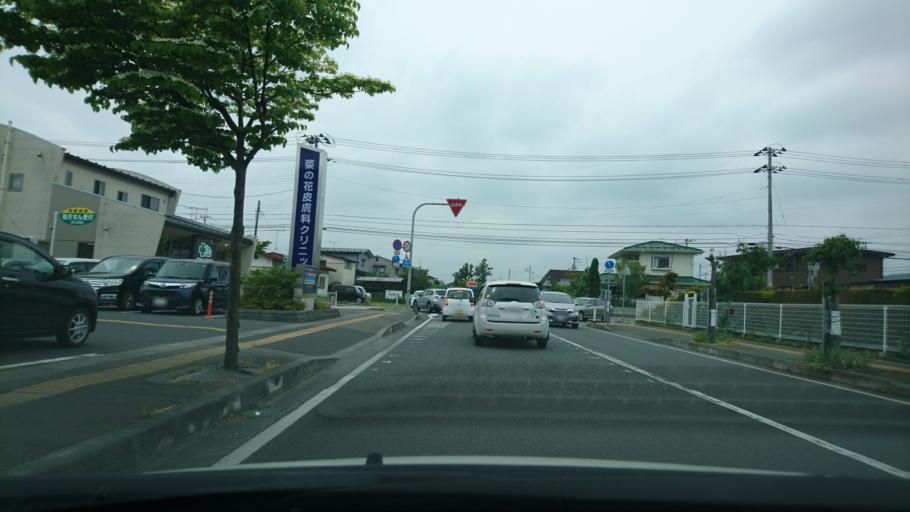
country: JP
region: Iwate
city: Ichinoseki
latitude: 38.9352
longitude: 141.1139
